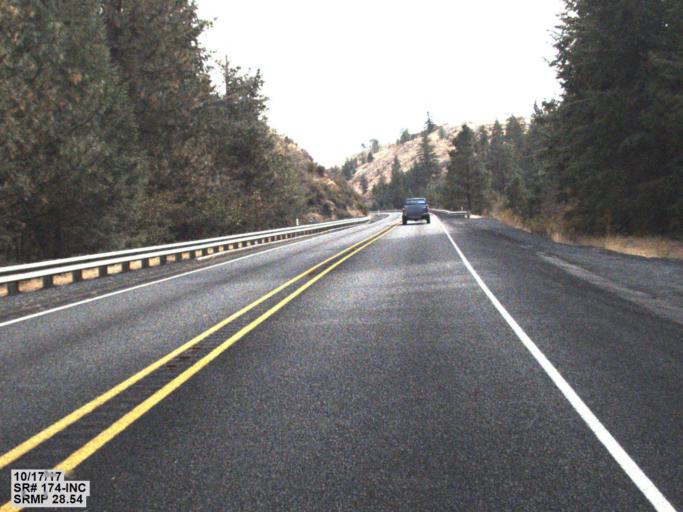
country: US
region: Washington
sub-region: Okanogan County
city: Coulee Dam
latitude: 47.9079
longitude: -118.8795
